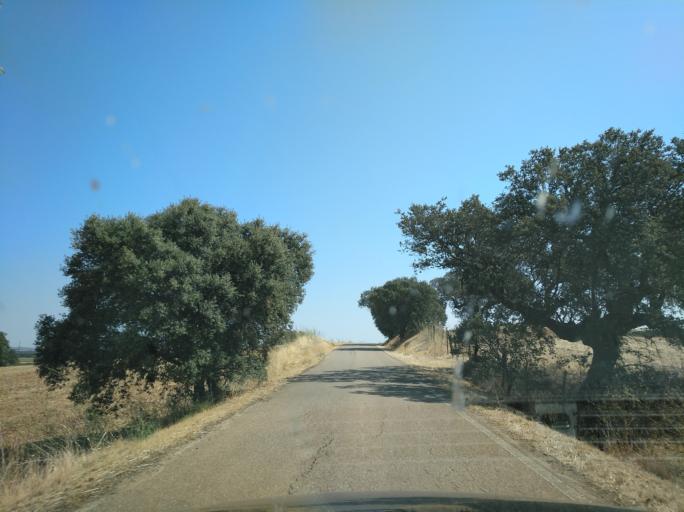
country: PT
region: Portalegre
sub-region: Campo Maior
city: Campo Maior
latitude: 39.0344
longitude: -6.9906
